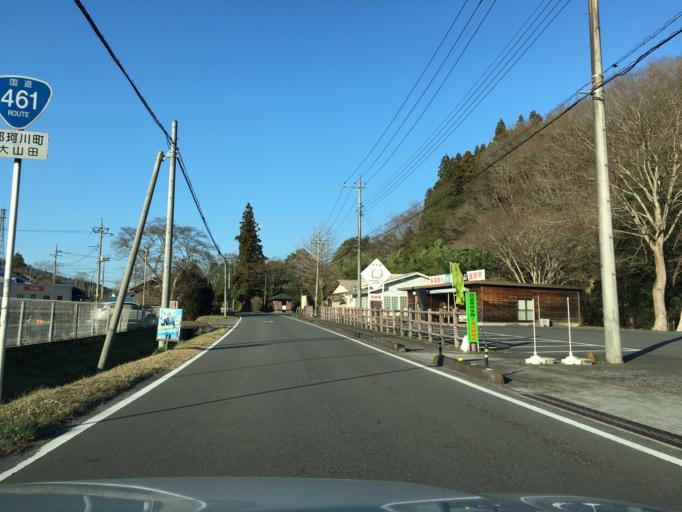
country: JP
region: Tochigi
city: Karasuyama
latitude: 36.7661
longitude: 140.2047
